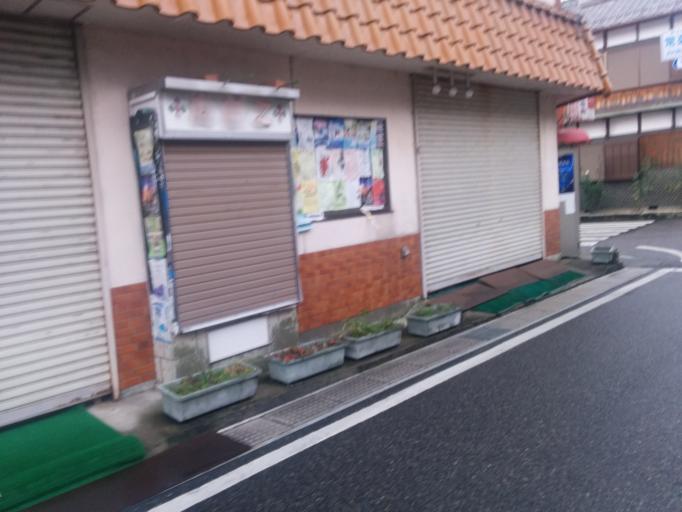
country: JP
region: Shiga Prefecture
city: Omihachiman
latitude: 35.1421
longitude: 136.1311
